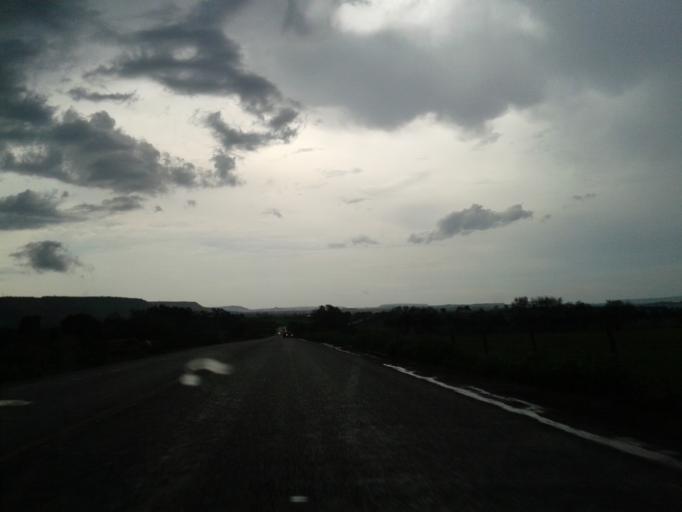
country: BR
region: Goias
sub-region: Quirinopolis
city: Quirinopolis
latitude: -18.4351
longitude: -50.4186
